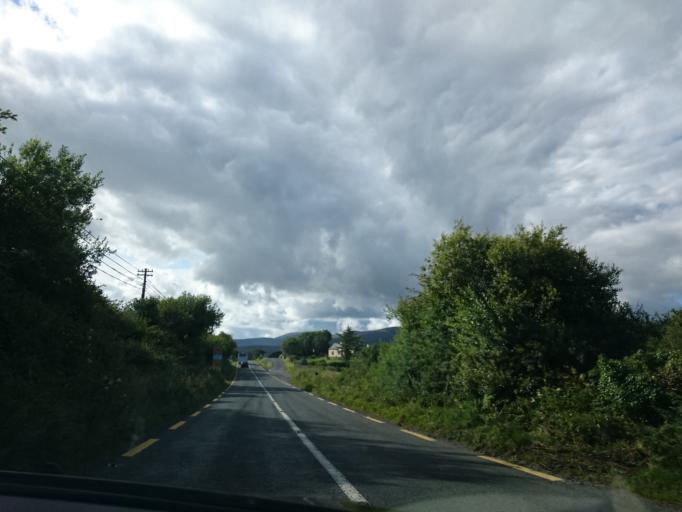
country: IE
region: Connaught
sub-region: Maigh Eo
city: Westport
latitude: 53.8979
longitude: -9.5604
